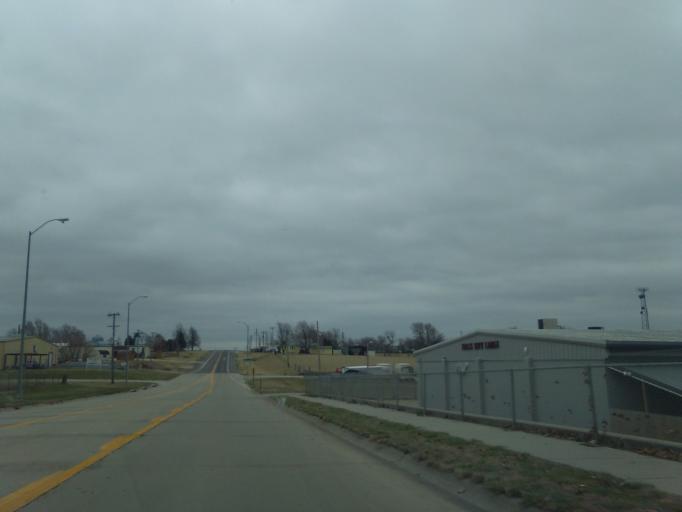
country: US
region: Nebraska
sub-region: Richardson County
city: Falls City
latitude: 40.0583
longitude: -95.5904
